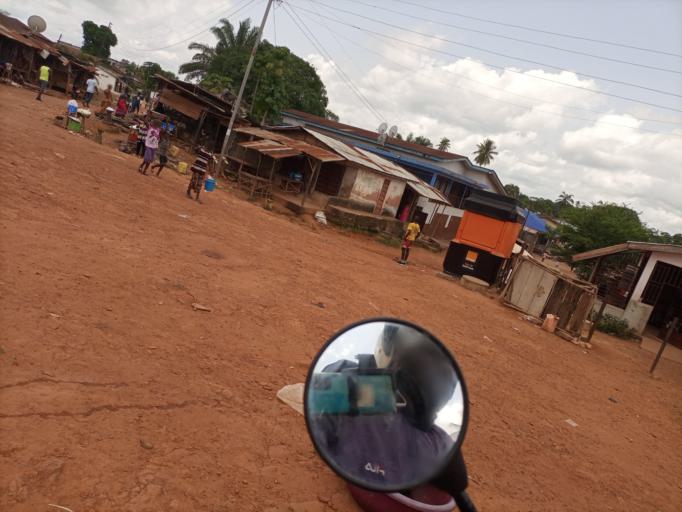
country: SL
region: Southern Province
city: Bo
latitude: 7.9562
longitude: -11.7340
